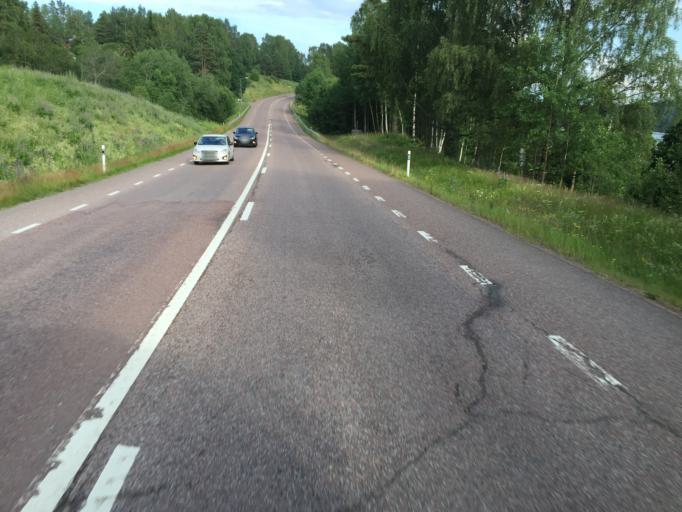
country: SE
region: Dalarna
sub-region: Borlange Kommun
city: Borlaenge
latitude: 60.5322
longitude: 15.3055
